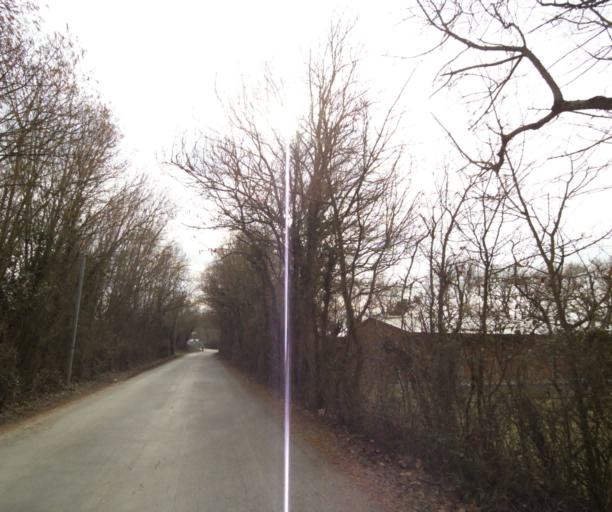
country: FR
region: Poitou-Charentes
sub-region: Departement des Deux-Sevres
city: Niort
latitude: 46.3028
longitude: -0.4518
